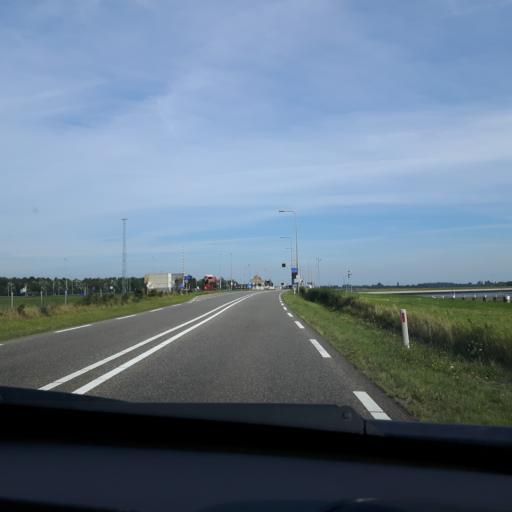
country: NL
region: Zeeland
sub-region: Gemeente Goes
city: Goes
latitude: 51.5422
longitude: 3.8658
